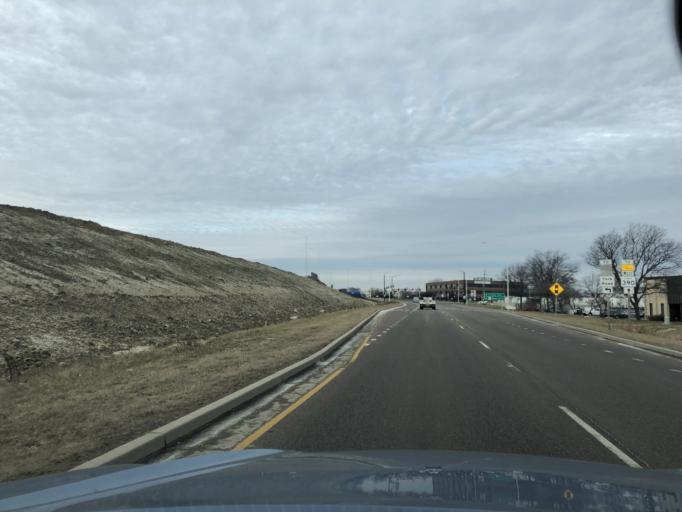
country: US
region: Illinois
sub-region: Cook County
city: Elk Grove Village
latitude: 41.9830
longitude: -87.9563
